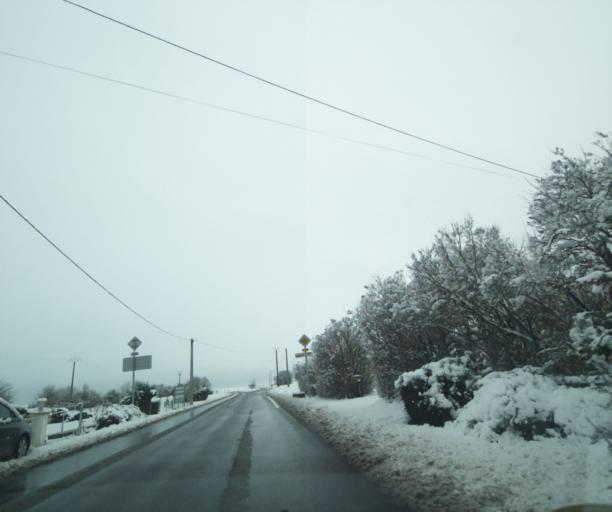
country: FR
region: Champagne-Ardenne
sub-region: Departement de la Haute-Marne
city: Montier-en-Der
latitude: 48.5316
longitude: 4.8163
